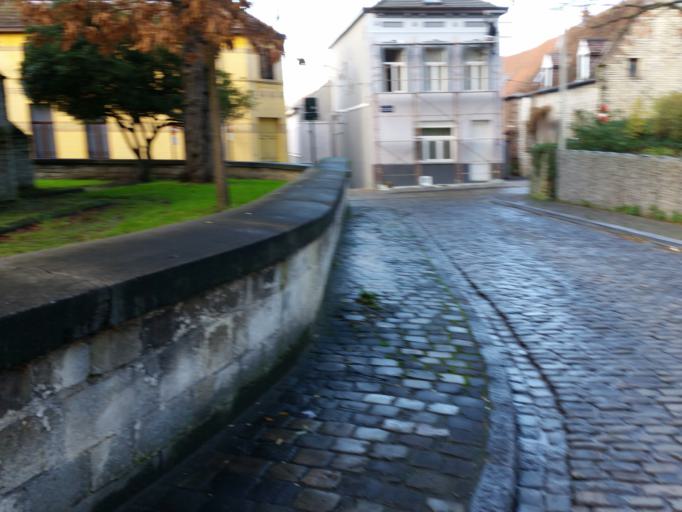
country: BE
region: Flanders
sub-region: Provincie Vlaams-Brabant
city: Diegem
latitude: 50.8929
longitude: 4.4178
